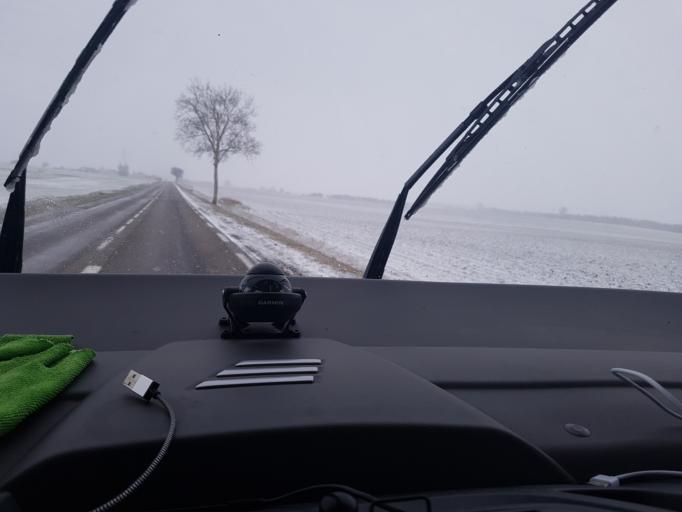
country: FR
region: Lorraine
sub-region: Departement de la Moselle
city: Solgne
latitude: 48.8969
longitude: 6.3586
